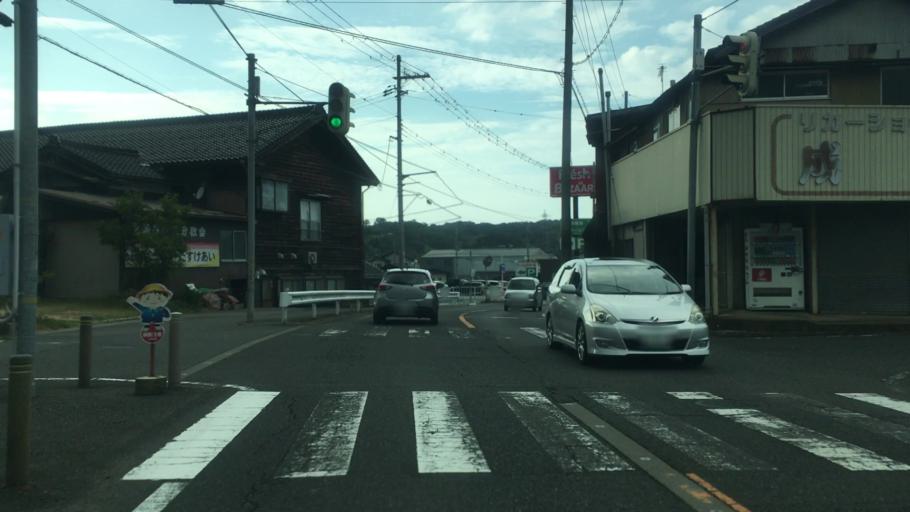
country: JP
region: Hyogo
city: Toyooka
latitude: 35.5239
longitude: 134.8217
